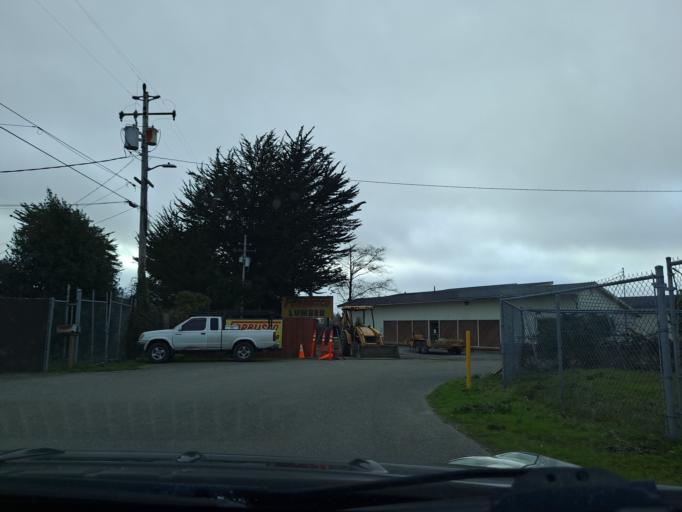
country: US
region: California
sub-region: Humboldt County
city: Fortuna
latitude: 40.5921
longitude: -124.1487
